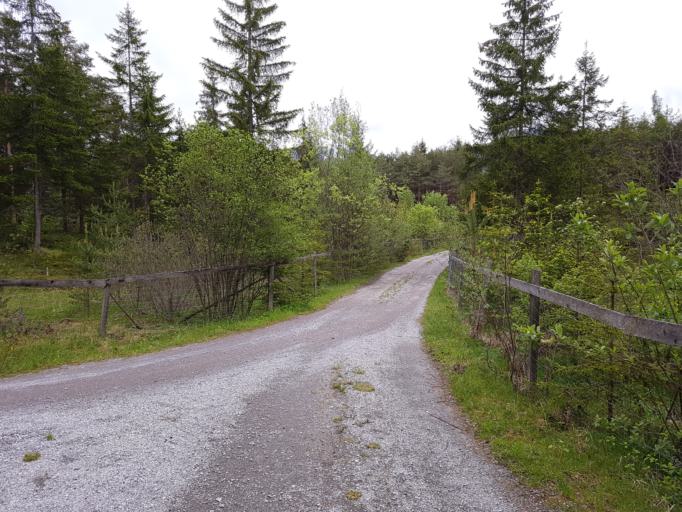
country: AT
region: Tyrol
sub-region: Politischer Bezirk Imst
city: Obsteig
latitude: 47.3013
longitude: 10.9445
